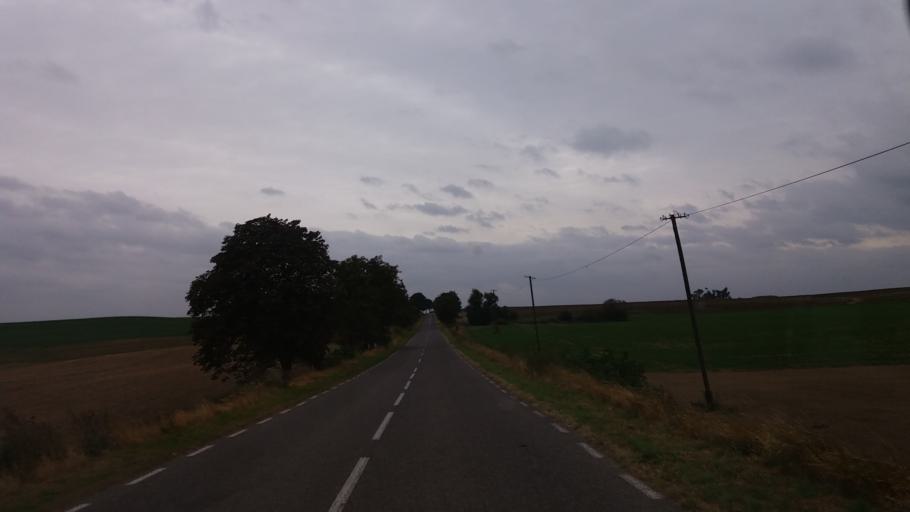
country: PL
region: Lubusz
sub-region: Powiat strzelecko-drezdenecki
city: Strzelce Krajenskie
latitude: 52.9429
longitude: 15.5634
